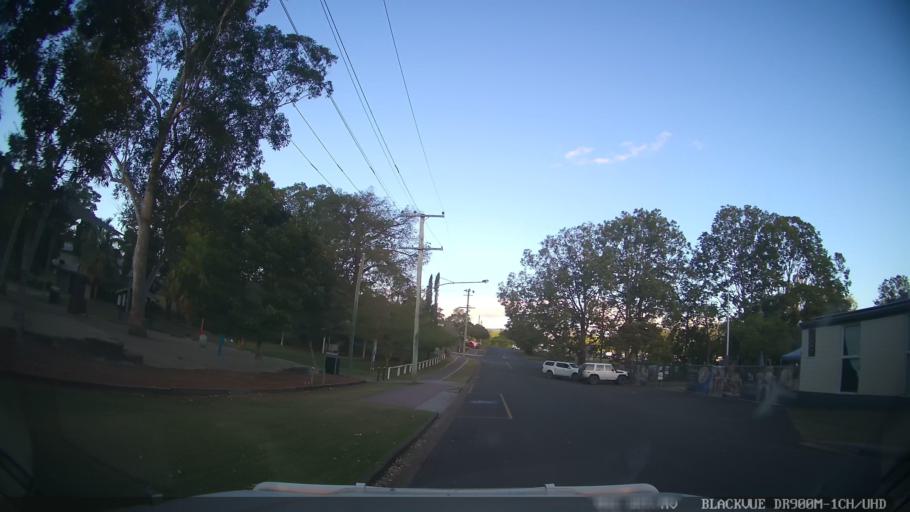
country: AU
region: Queensland
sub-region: Sunshine Coast
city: Yandina
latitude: -26.5966
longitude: 152.7265
